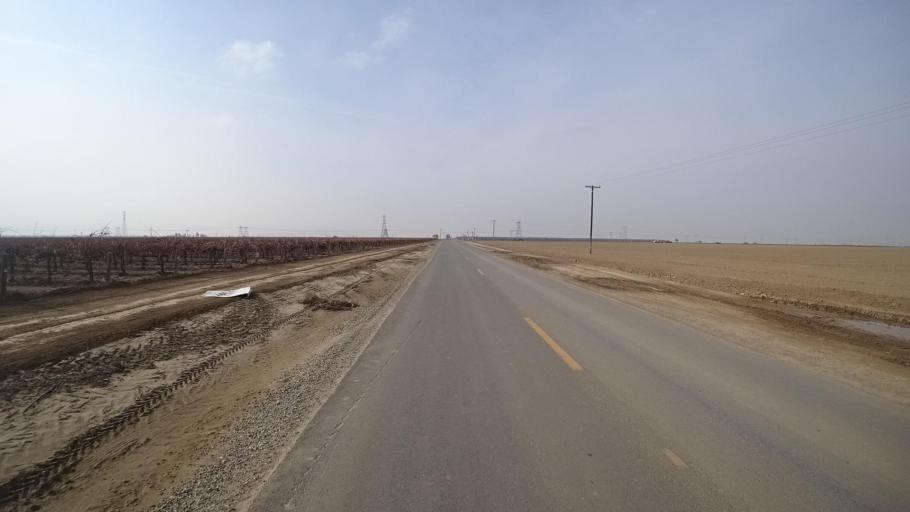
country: US
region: California
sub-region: Kern County
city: Arvin
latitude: 35.0449
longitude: -118.8690
